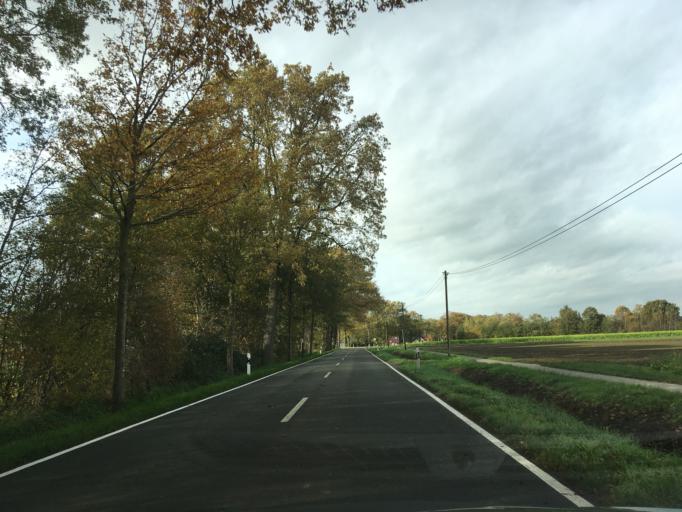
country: DE
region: North Rhine-Westphalia
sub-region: Regierungsbezirk Munster
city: Vreden
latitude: 52.0852
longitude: 6.8949
